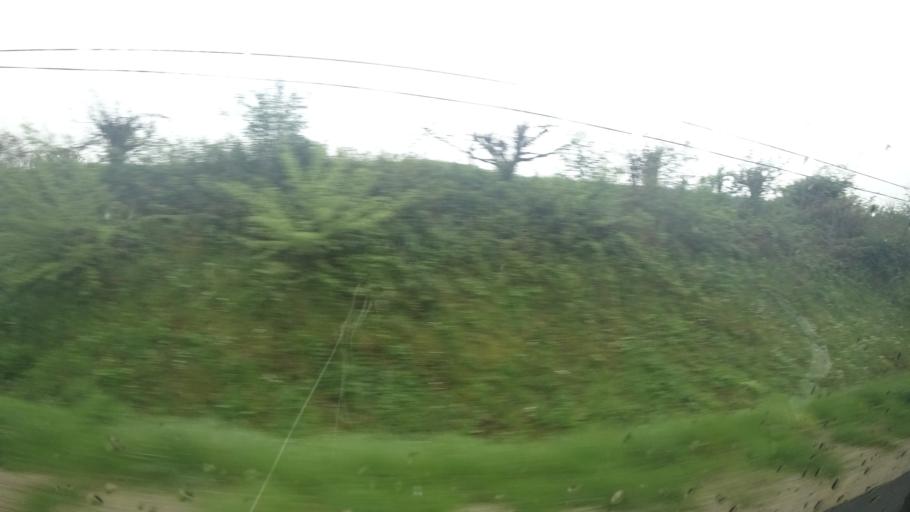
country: FR
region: Midi-Pyrenees
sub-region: Departement de l'Aveyron
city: Laissac
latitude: 44.2788
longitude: 2.8615
